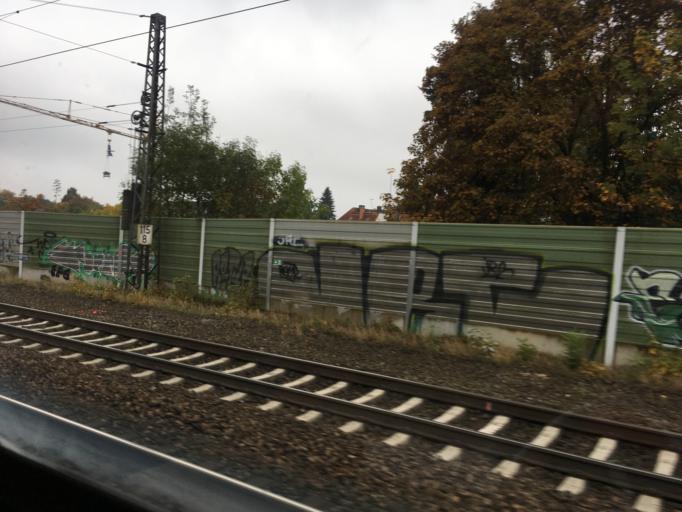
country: DE
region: Lower Saxony
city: Osnabrueck
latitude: 52.2622
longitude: 8.0417
